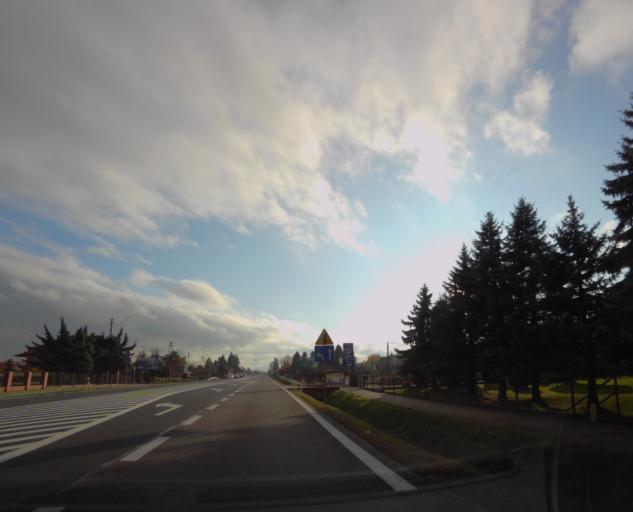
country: PL
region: Subcarpathian Voivodeship
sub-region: Powiat przemyski
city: Orly
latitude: 49.8607
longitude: 22.8075
